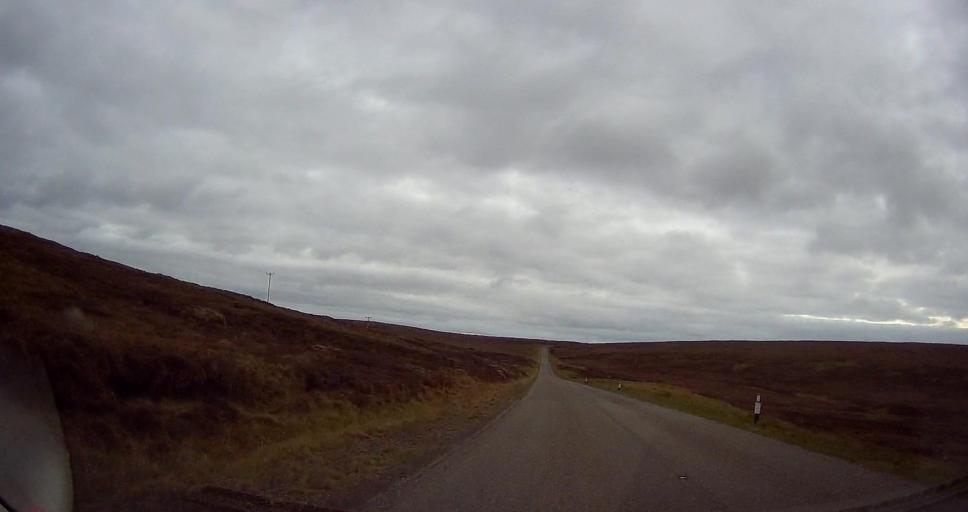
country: GB
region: Scotland
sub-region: Shetland Islands
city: Shetland
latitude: 60.6693
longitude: -1.0107
